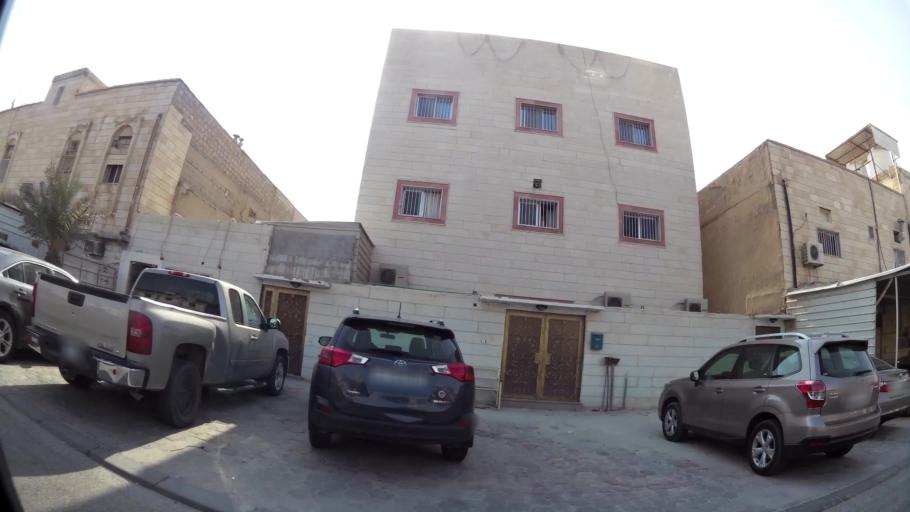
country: KW
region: Muhafazat al Jahra'
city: Al Jahra'
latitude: 29.3507
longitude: 47.6810
